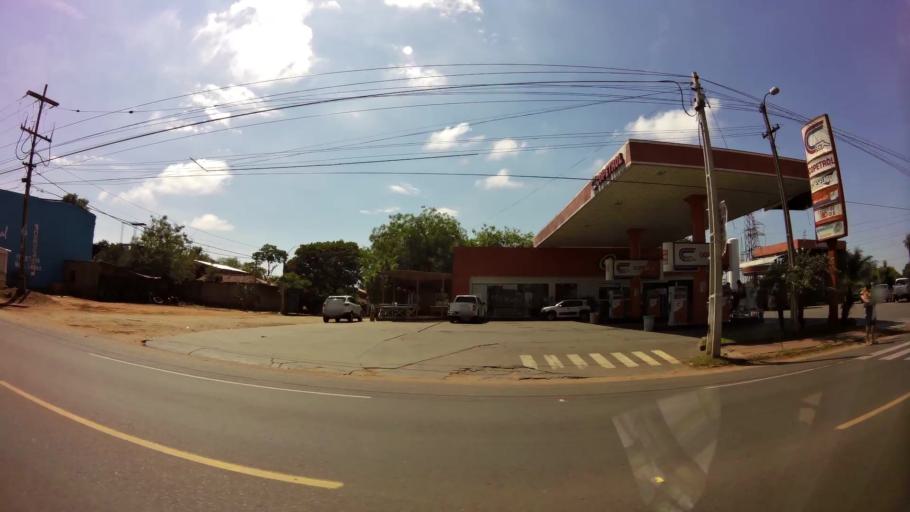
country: PY
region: Central
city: San Lorenzo
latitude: -25.3207
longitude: -57.5083
